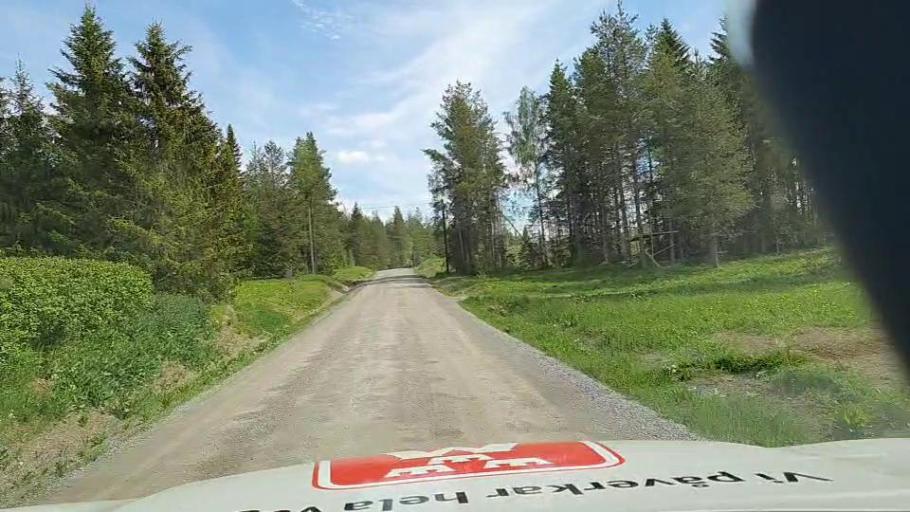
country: SE
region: Jaemtland
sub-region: OEstersunds Kommun
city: Brunflo
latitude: 63.0131
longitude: 14.7789
